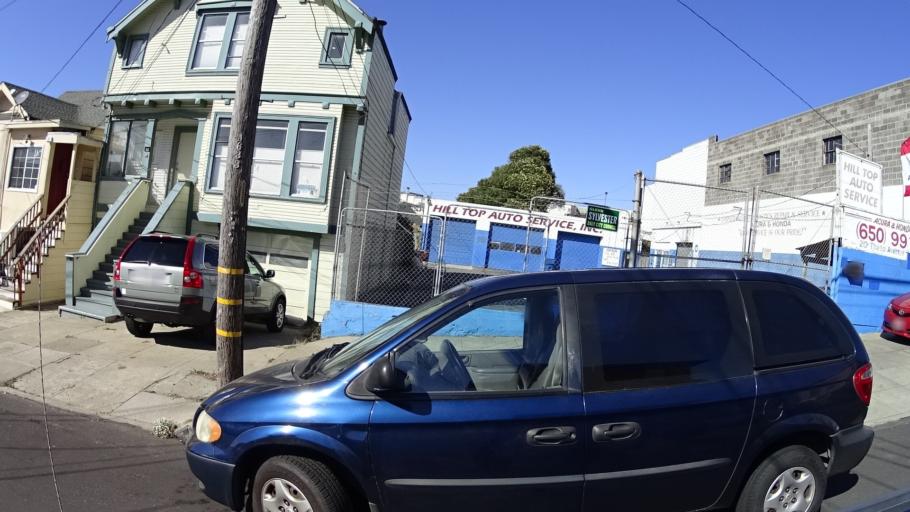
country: US
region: California
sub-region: San Mateo County
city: Daly City
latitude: 37.7042
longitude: -122.4633
